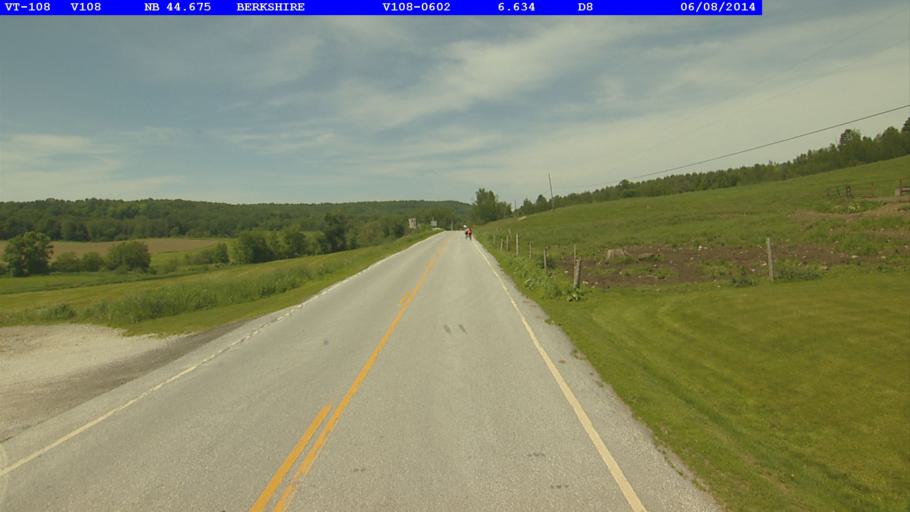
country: US
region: Vermont
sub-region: Franklin County
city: Enosburg Falls
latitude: 45.0126
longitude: -72.8251
